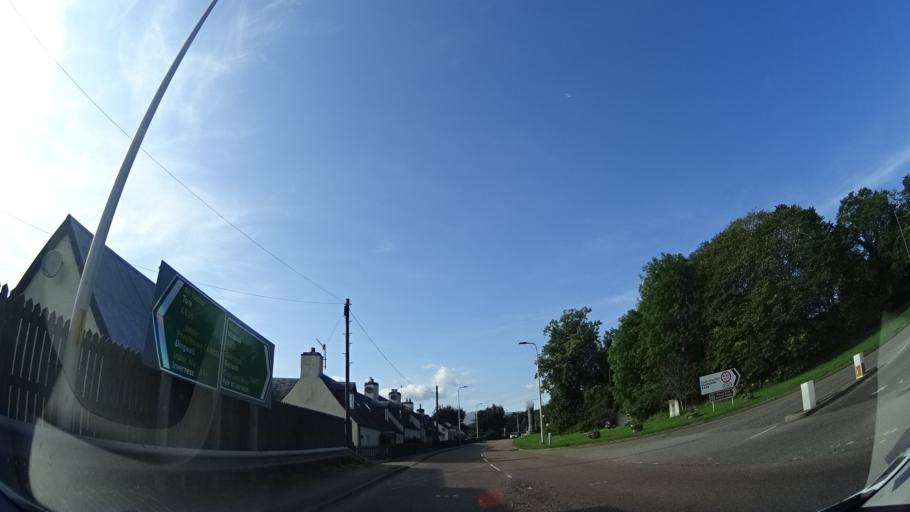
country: GB
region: Scotland
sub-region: Highland
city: Muir of Ord
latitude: 57.5654
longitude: -4.5784
